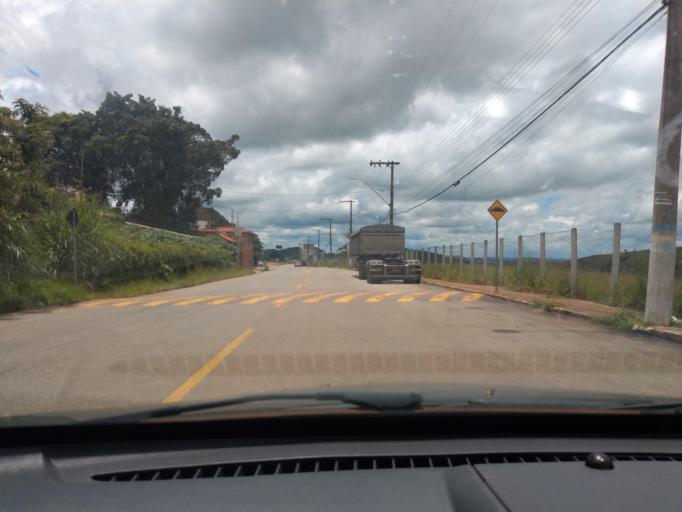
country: BR
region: Minas Gerais
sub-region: Lavras
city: Lavras
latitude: -21.2401
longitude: -45.0232
